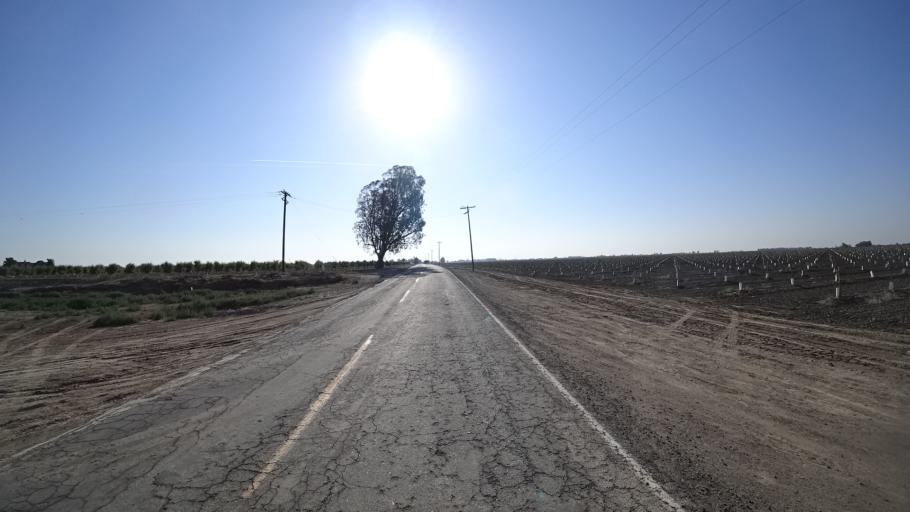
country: US
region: California
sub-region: Fresno County
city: Riverdale
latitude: 36.3802
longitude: -119.9213
